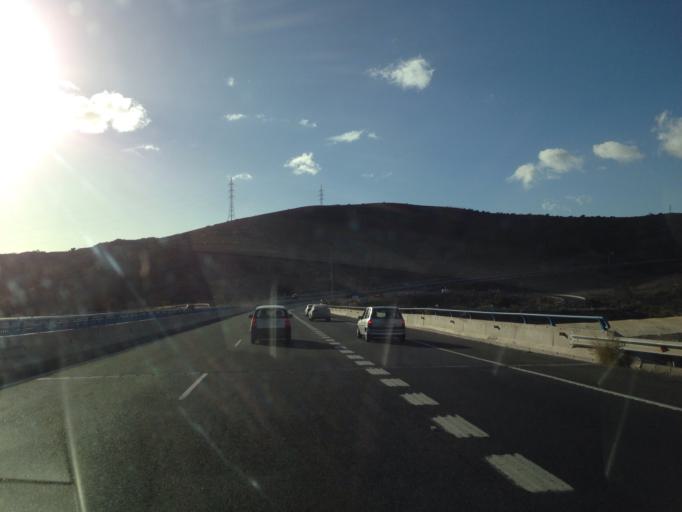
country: ES
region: Canary Islands
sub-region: Provincia de Las Palmas
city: Puerto Rico
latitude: 27.7658
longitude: -15.6697
